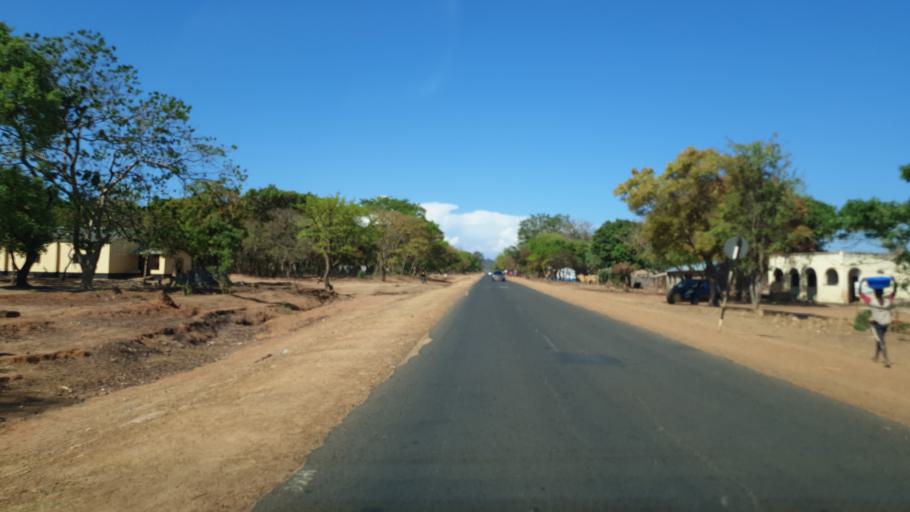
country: MW
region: Central Region
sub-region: Salima District
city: Salima
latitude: -13.7441
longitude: 34.5927
